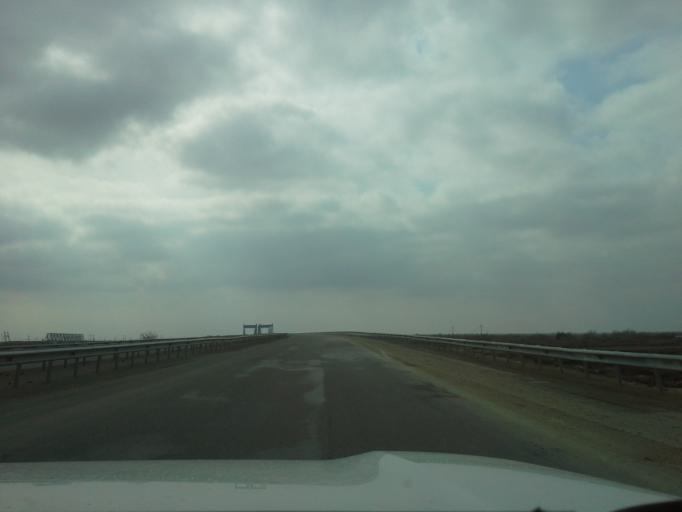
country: TM
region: Ahal
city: Tejen
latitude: 37.2369
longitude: 60.1625
